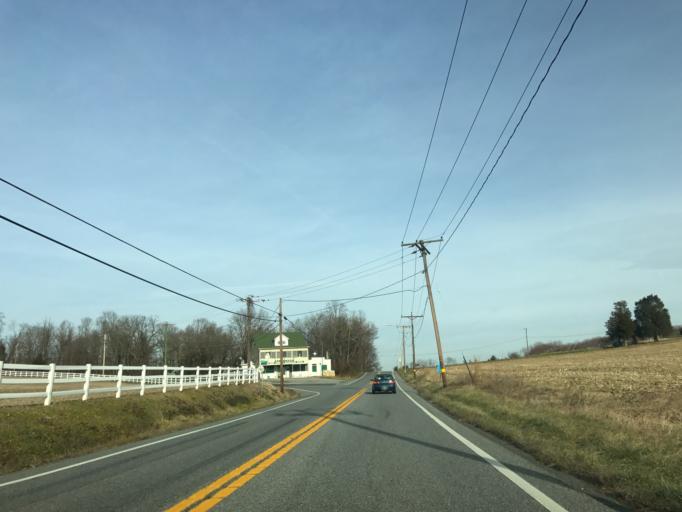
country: US
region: Maryland
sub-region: Baltimore County
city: Perry Hall
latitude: 39.4344
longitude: -76.4880
